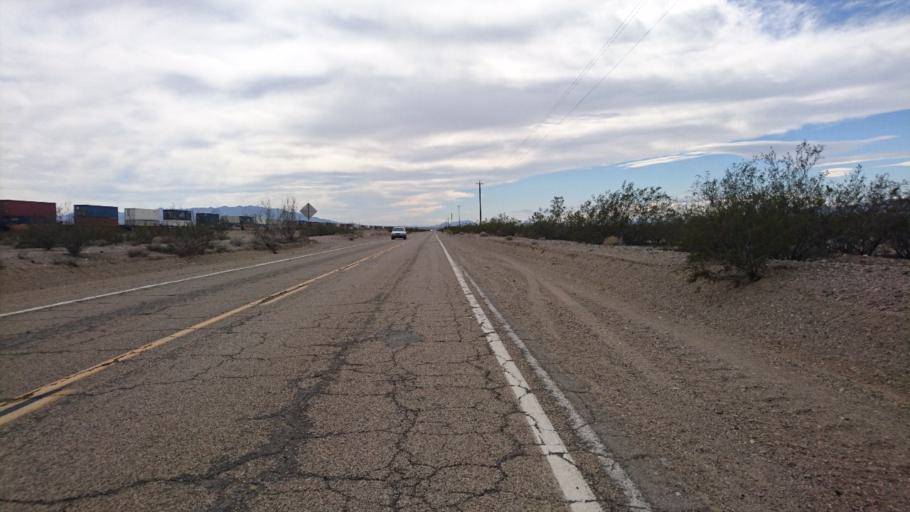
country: US
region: California
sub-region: San Bernardino County
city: Needles
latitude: 34.7978
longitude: -115.1972
